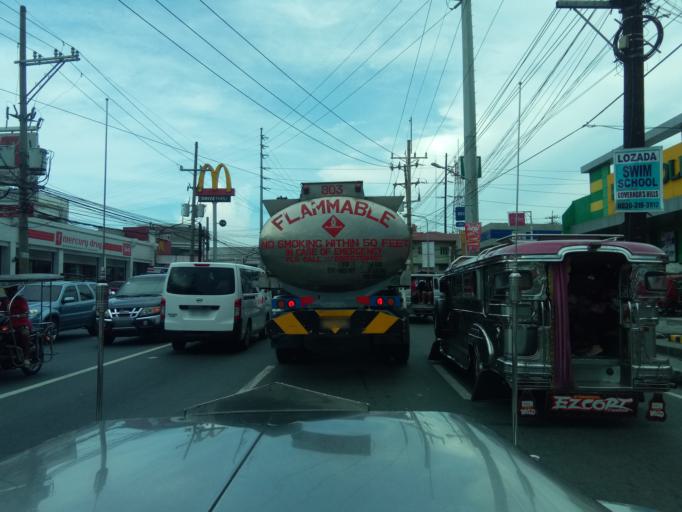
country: PH
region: Calabarzon
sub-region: Province of Cavite
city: Manggahan
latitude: 14.2913
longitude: 120.9098
